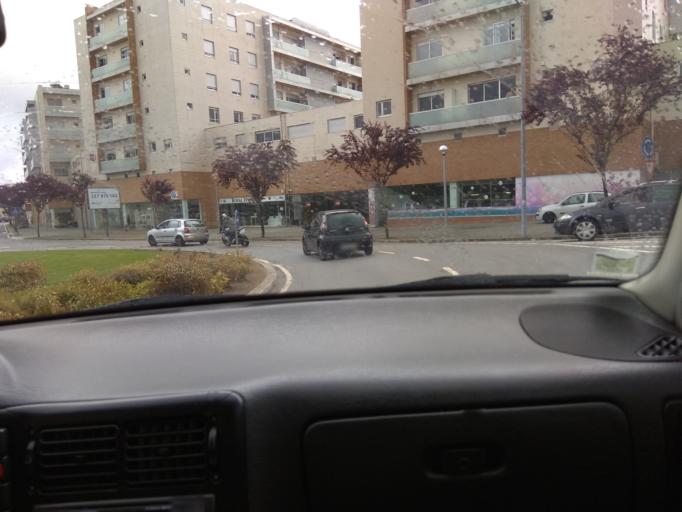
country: PT
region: Porto
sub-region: Maia
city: Leca do Bailio
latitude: 41.2257
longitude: -8.6108
